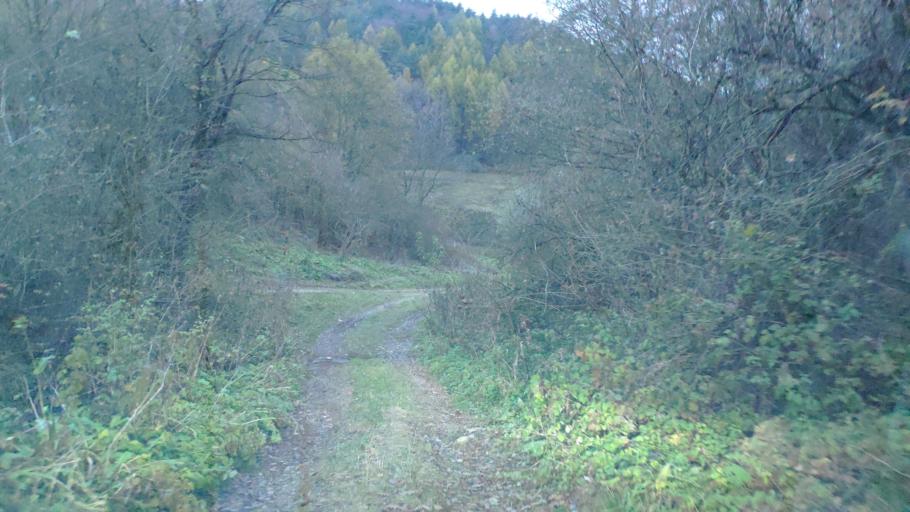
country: SK
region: Kosicky
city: Gelnica
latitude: 48.9392
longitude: 21.0794
